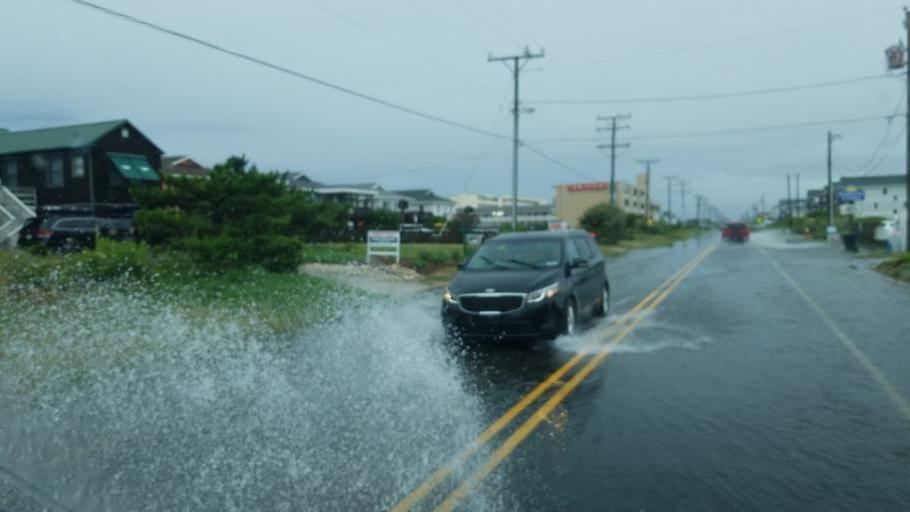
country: US
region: North Carolina
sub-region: Dare County
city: Kill Devil Hills
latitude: 36.0363
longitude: -75.6708
